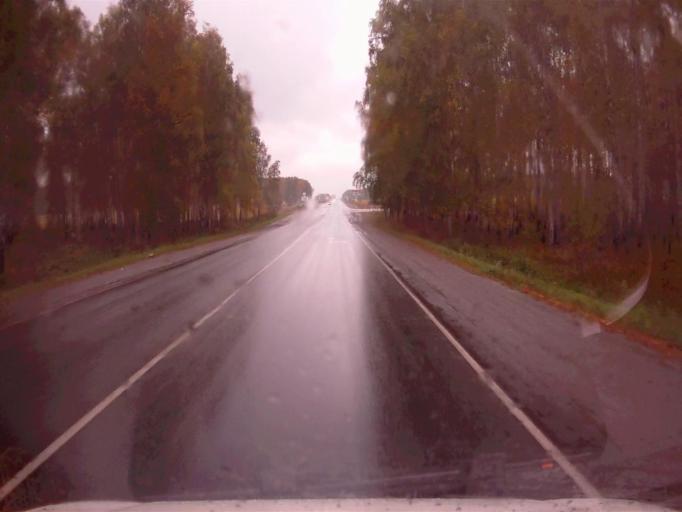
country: RU
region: Chelyabinsk
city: Argayash
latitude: 55.4153
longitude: 61.0306
